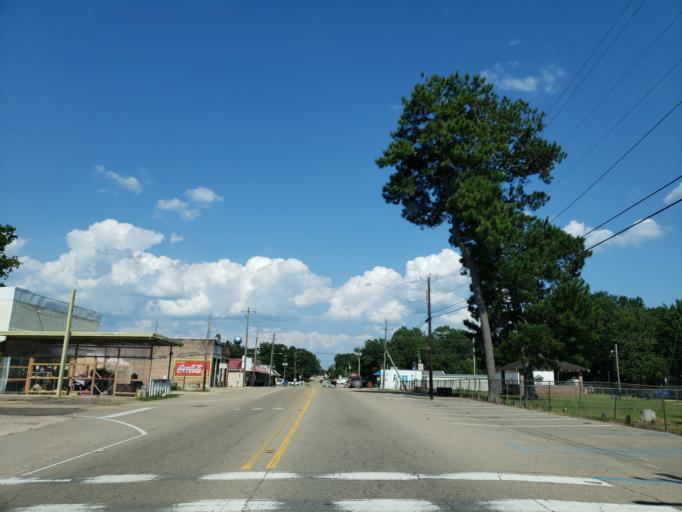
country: US
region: Mississippi
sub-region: Covington County
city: Collins
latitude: 31.5617
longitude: -89.4996
